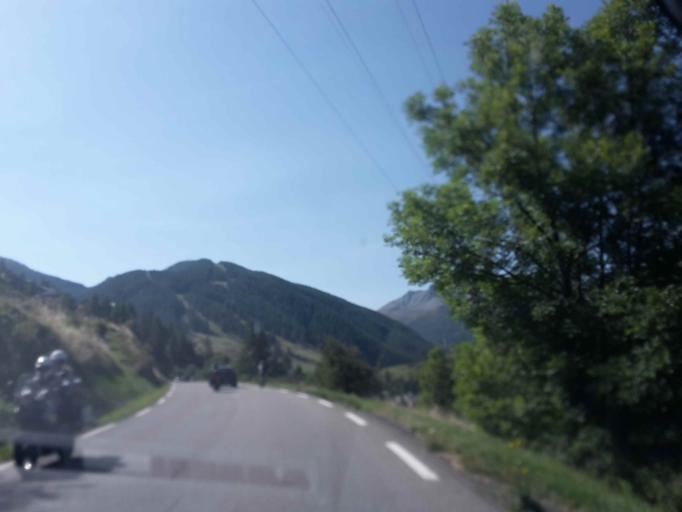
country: FR
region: Provence-Alpes-Cote d'Azur
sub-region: Departement des Hautes-Alpes
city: Guillestre
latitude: 44.6020
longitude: 6.6890
